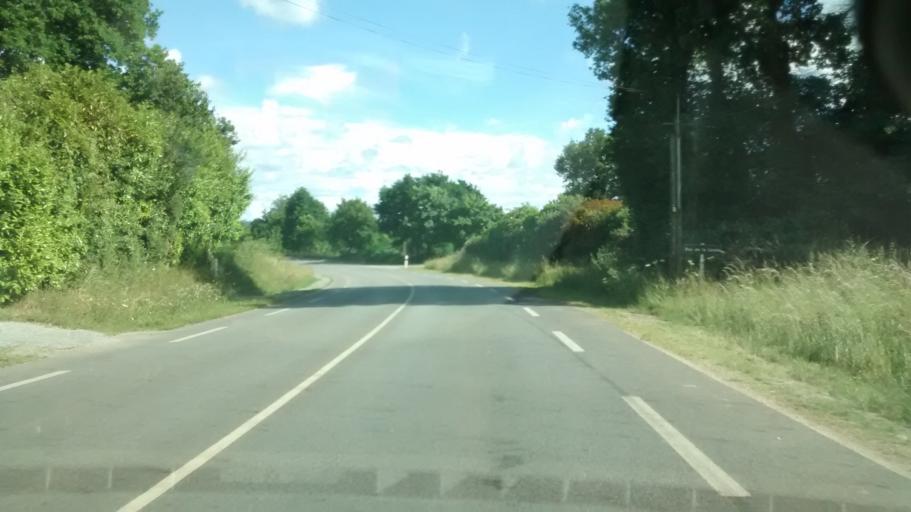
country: FR
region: Brittany
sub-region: Departement du Morbihan
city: Malestroit
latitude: 47.8429
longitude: -2.4150
